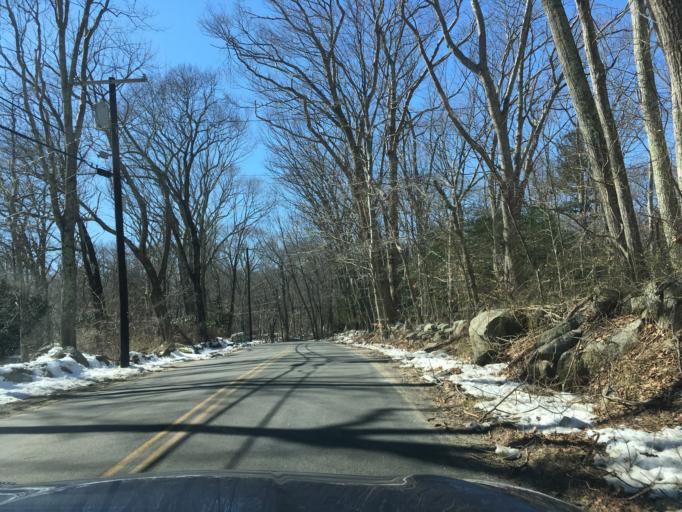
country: US
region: Rhode Island
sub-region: Washington County
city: Exeter
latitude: 41.6079
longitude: -71.5146
